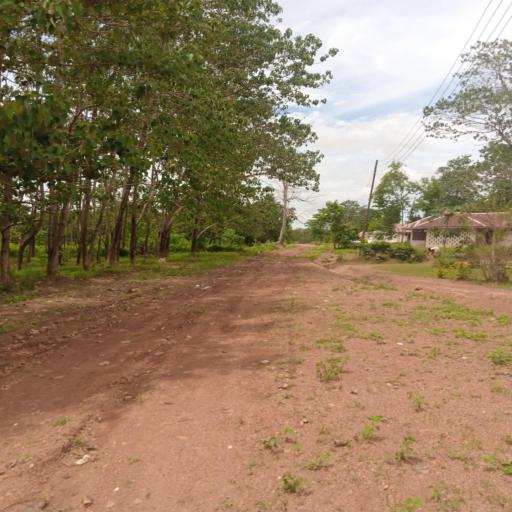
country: SL
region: Southern Province
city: Largo
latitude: 8.1119
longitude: -12.0793
